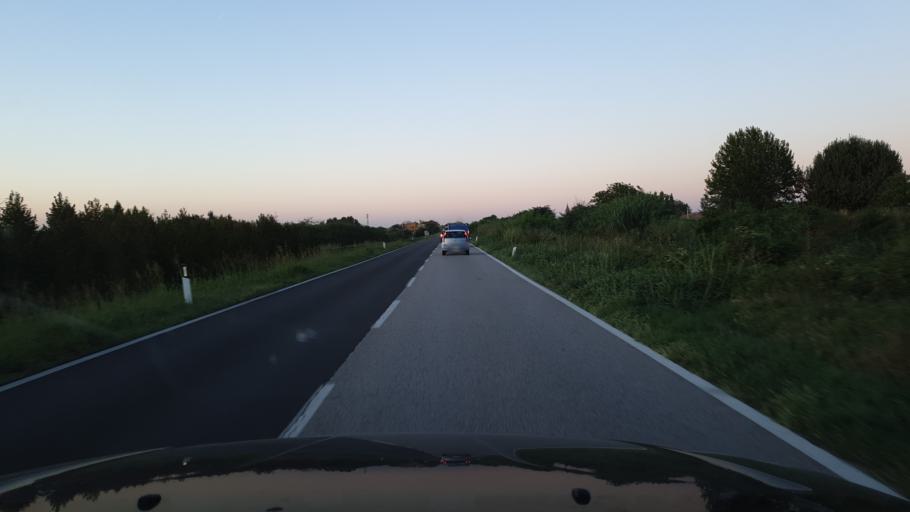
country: IT
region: Emilia-Romagna
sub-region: Provincia di Bologna
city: Ca De Fabbri
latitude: 44.6136
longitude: 11.4494
